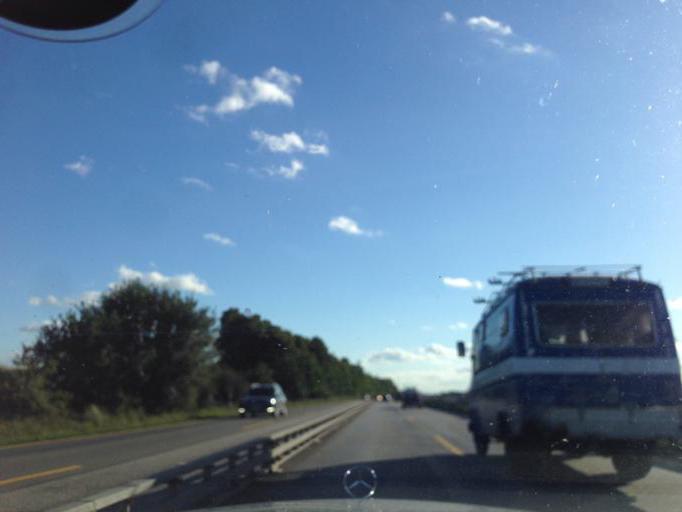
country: DE
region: Schleswig-Holstein
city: Loop
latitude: 54.1351
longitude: 9.9605
